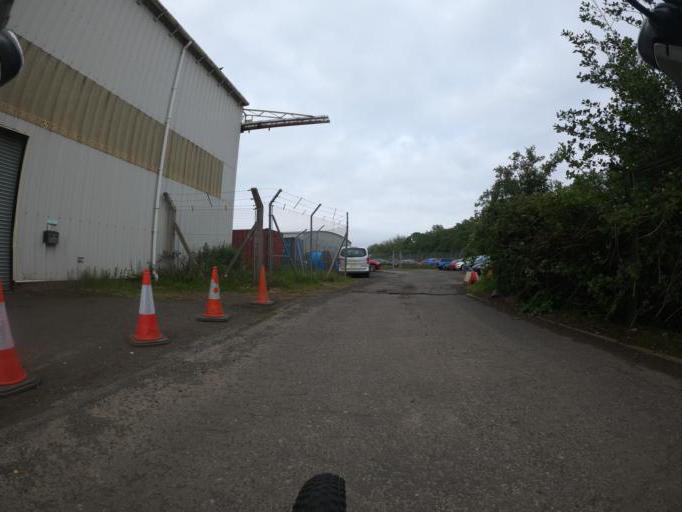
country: GB
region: Scotland
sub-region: Edinburgh
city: Ratho
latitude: 55.9444
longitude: -3.3496
